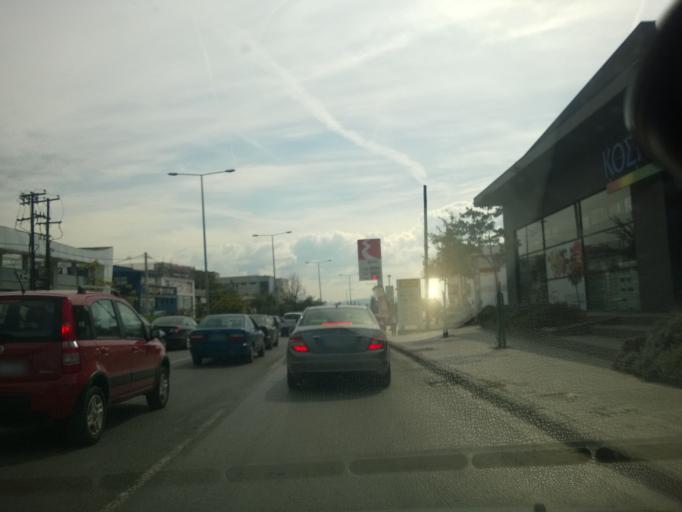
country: GR
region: Central Macedonia
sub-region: Nomos Thessalonikis
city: Kalamaria
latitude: 40.5796
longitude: 22.9676
